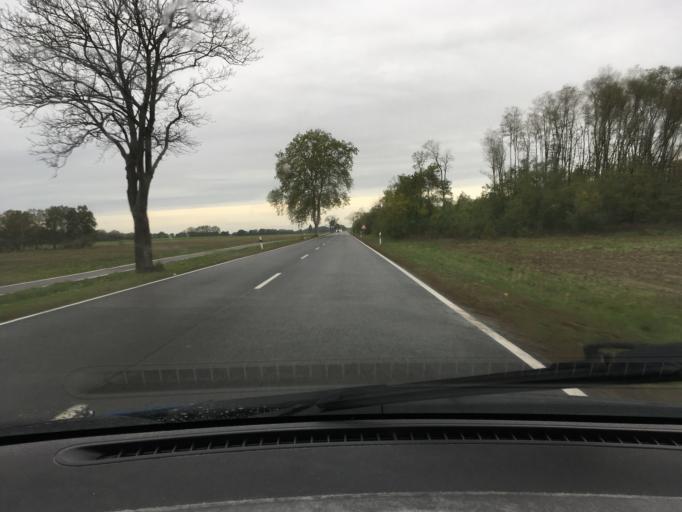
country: DE
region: Saxony-Anhalt
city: Rodleben
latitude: 51.9262
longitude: 12.1545
